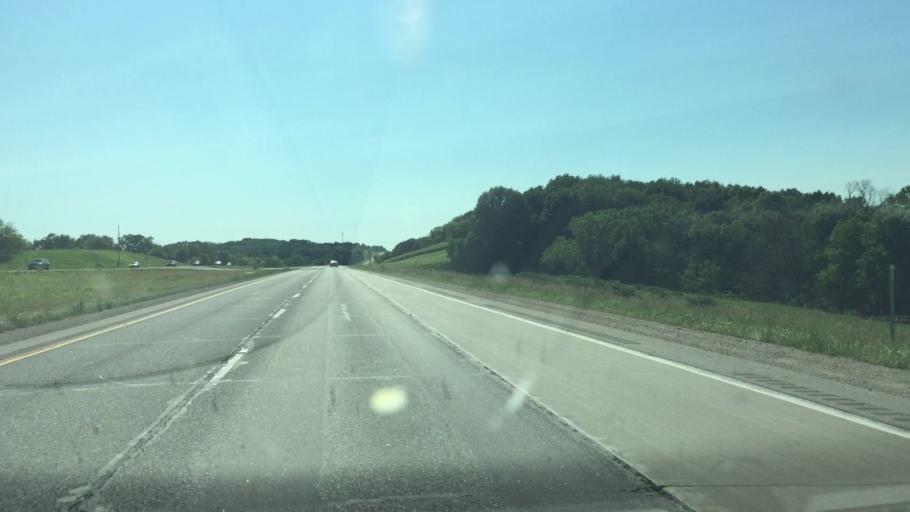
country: US
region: Iowa
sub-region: Linn County
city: Ely
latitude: 41.9257
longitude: -91.5666
